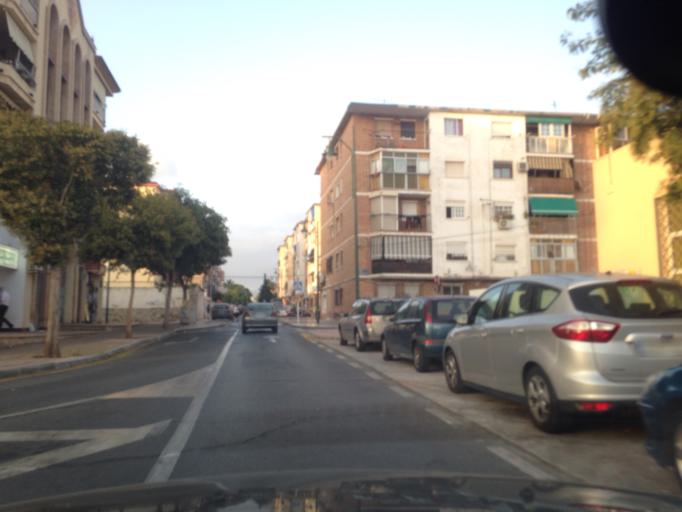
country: ES
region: Andalusia
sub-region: Provincia de Malaga
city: Malaga
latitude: 36.7200
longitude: -4.4544
